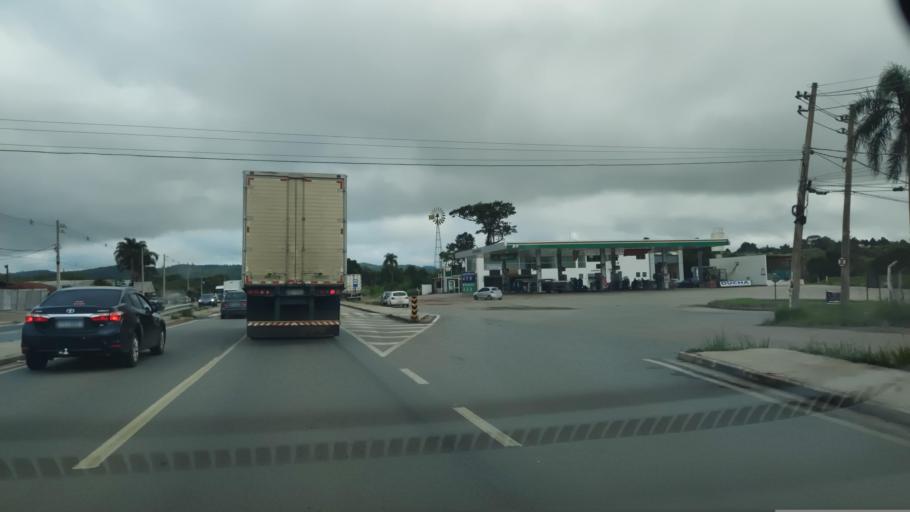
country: BR
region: Sao Paulo
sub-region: Vargem Grande Paulista
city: Vargem Grande Paulista
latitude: -23.6332
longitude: -47.0552
